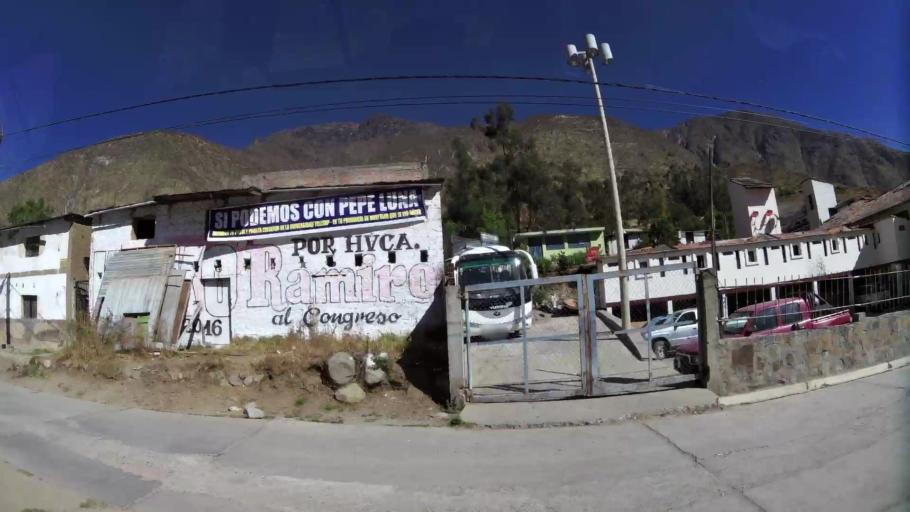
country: PE
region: Huancavelica
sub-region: Huaytara
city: Quito-Arma
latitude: -13.6042
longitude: -75.3506
